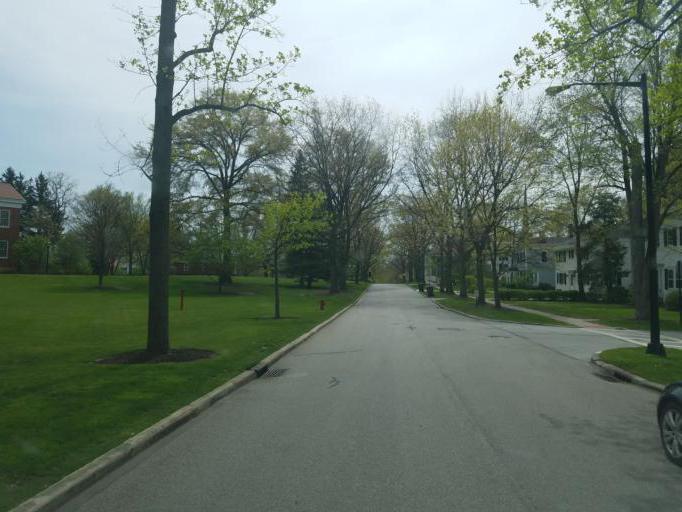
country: US
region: Ohio
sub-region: Summit County
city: Hudson
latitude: 41.2448
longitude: -81.4376
